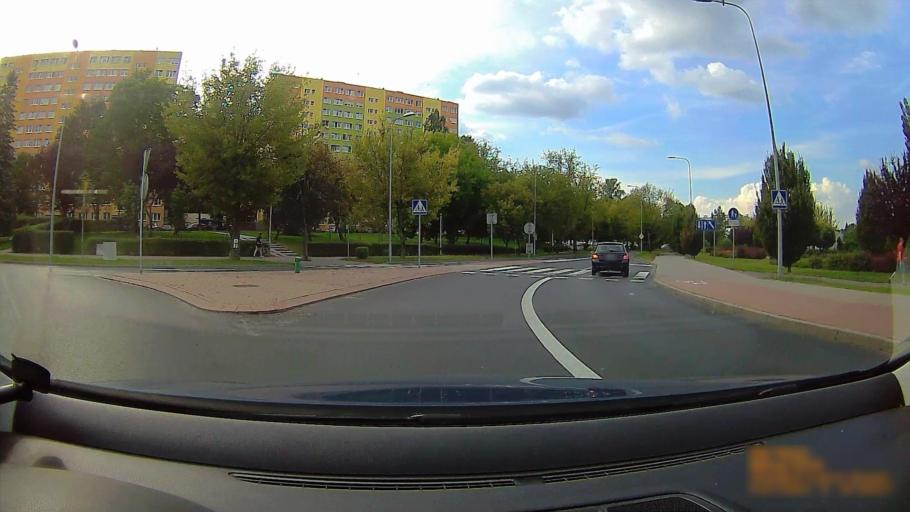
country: PL
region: Greater Poland Voivodeship
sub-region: Konin
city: Konin
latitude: 52.2298
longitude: 18.2813
